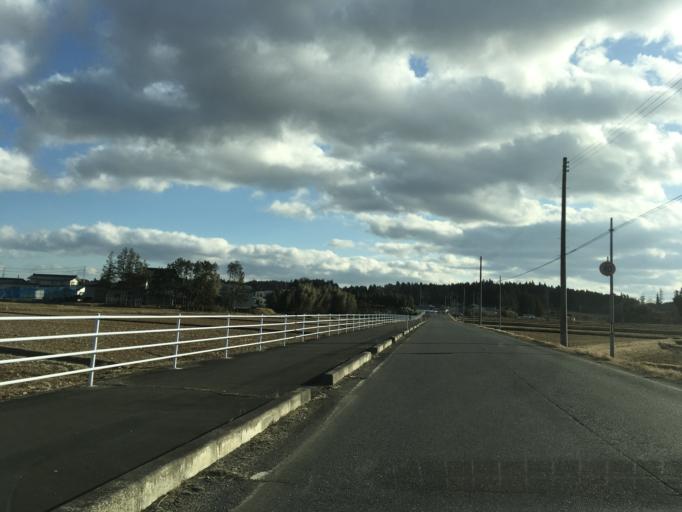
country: JP
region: Iwate
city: Ichinoseki
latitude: 38.8242
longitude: 141.0012
